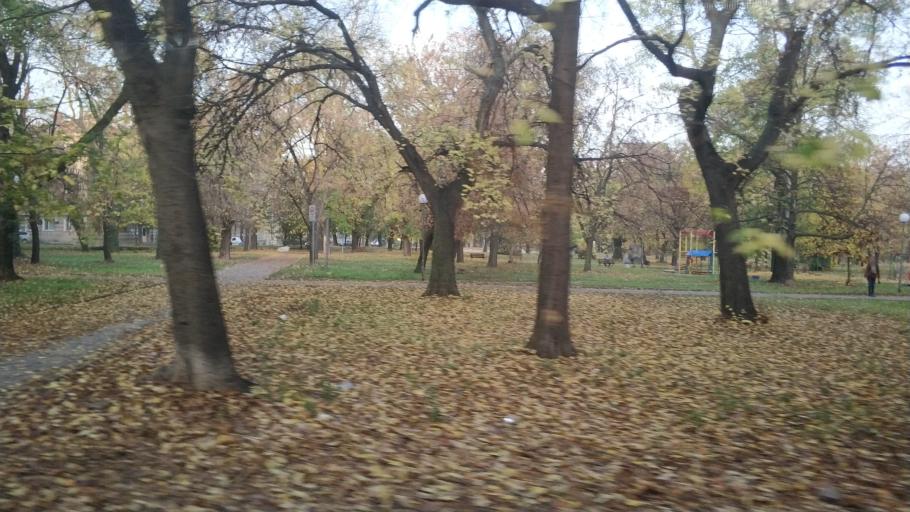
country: BG
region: Stara Zagora
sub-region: Obshtina Stara Zagora
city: Stara Zagora
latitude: 42.4185
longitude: 25.6267
